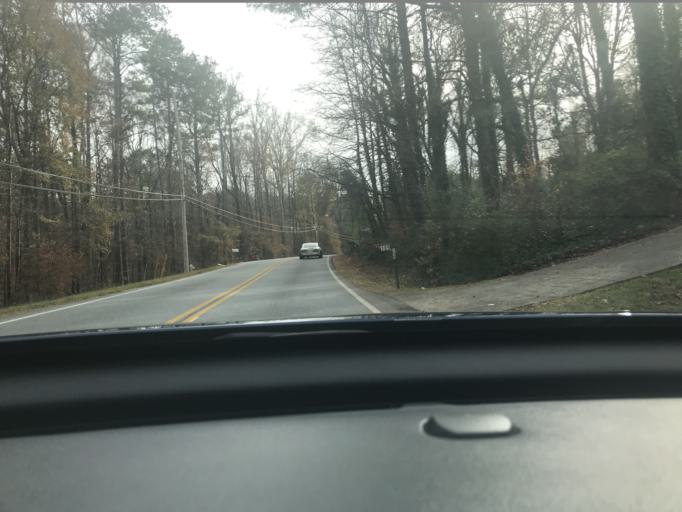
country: US
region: Georgia
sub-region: Gwinnett County
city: Lilburn
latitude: 33.8954
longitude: -84.0957
